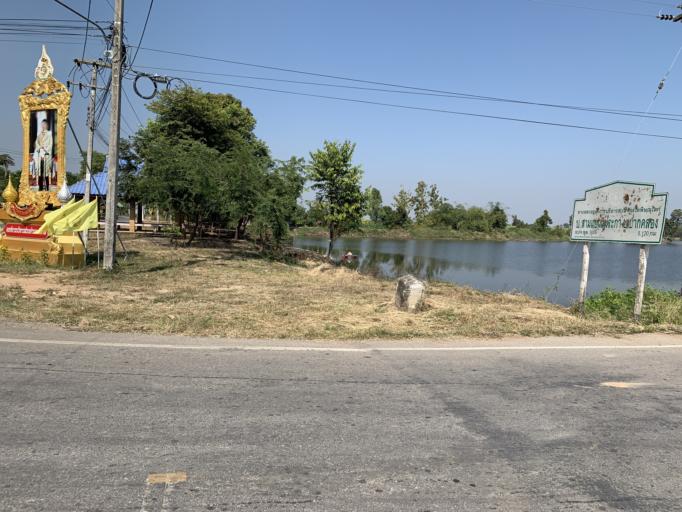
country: TH
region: Phitsanulok
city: Bang Krathum
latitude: 16.6843
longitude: 100.3314
